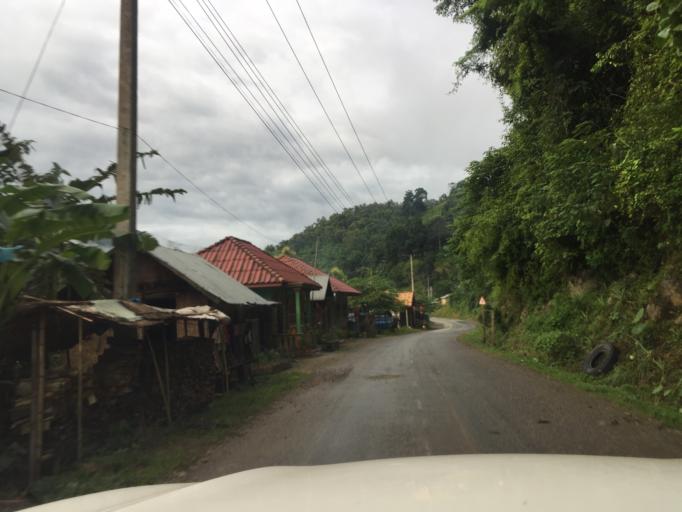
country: LA
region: Oudomxai
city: Muang La
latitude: 21.0567
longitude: 102.2408
